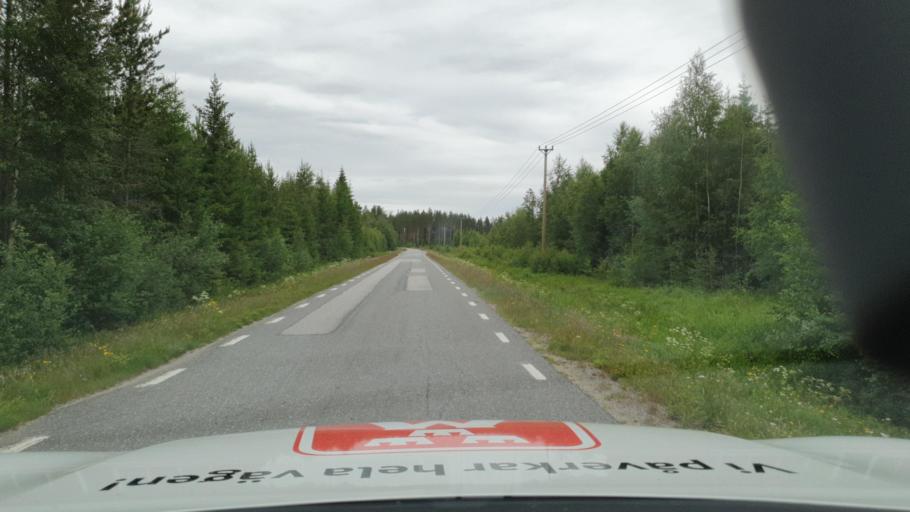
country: SE
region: Vaesterbotten
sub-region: Nordmalings Kommun
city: Nordmaling
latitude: 63.5149
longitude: 19.4213
